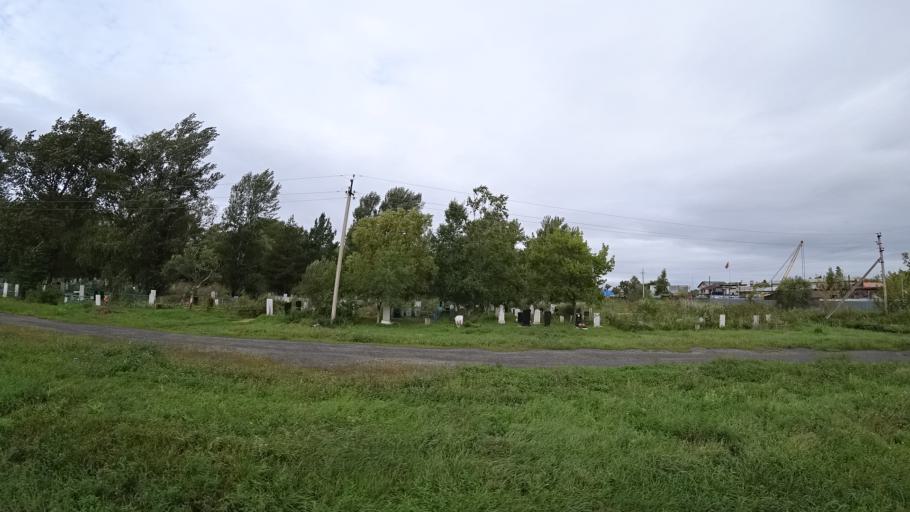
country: RU
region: Primorskiy
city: Chernigovka
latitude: 44.3316
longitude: 132.5744
